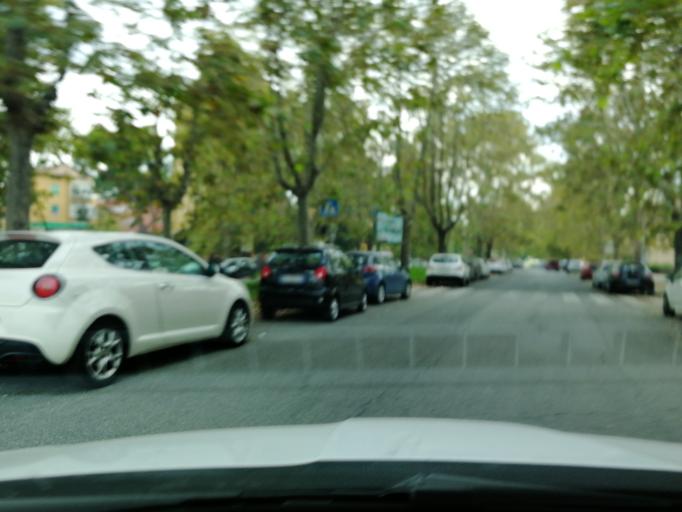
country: IT
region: Latium
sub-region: Citta metropolitana di Roma Capitale
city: Rome
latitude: 41.8599
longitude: 12.5506
